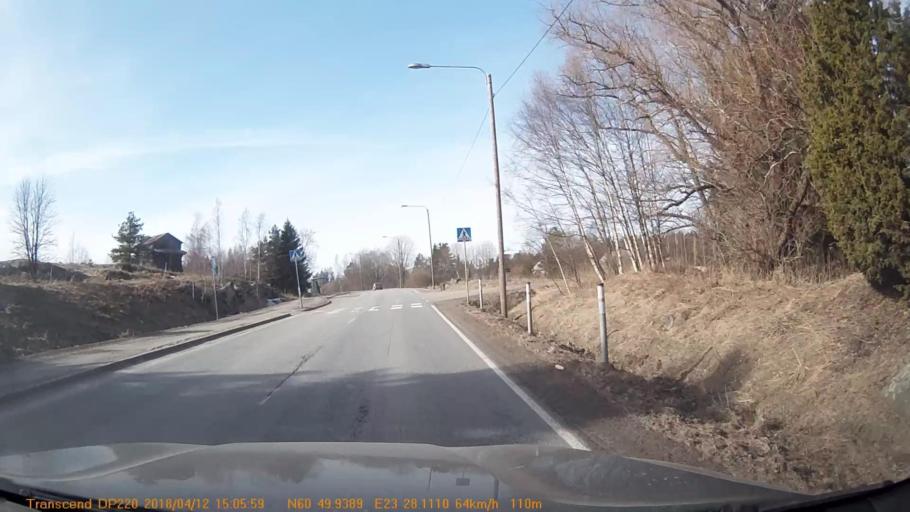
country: FI
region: Haeme
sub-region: Forssa
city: Jokioinen
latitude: 60.8324
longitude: 23.4684
